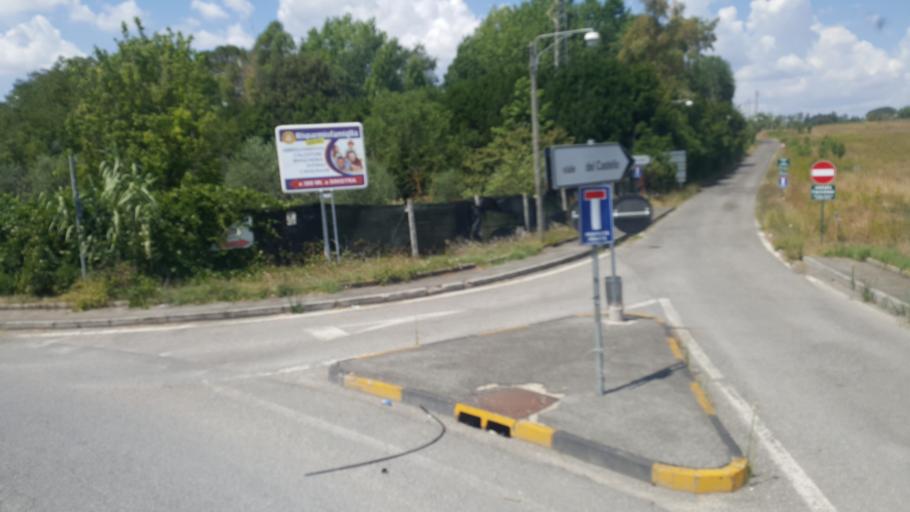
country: IT
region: Latium
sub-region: Citta metropolitana di Roma Capitale
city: Bivio di Capanelle
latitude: 42.1260
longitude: 12.5963
